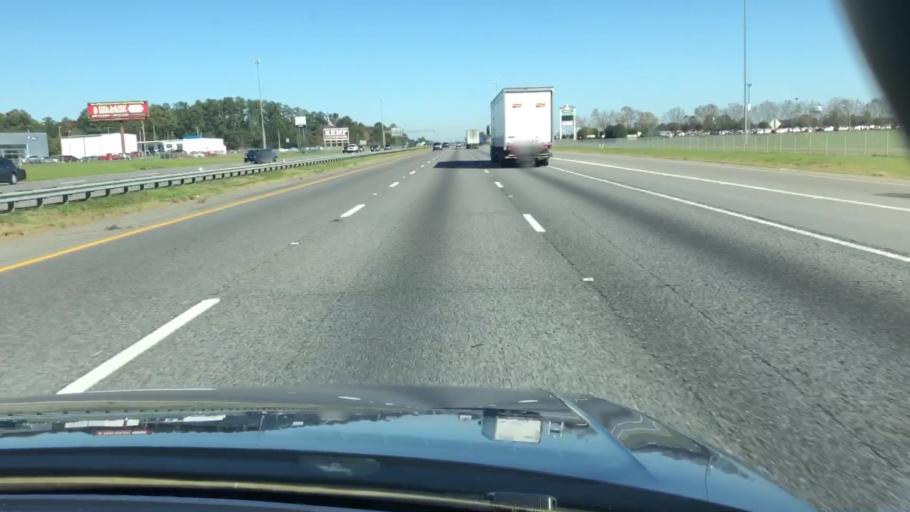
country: US
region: Georgia
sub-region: Houston County
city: Perry
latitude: 32.4353
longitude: -83.7562
